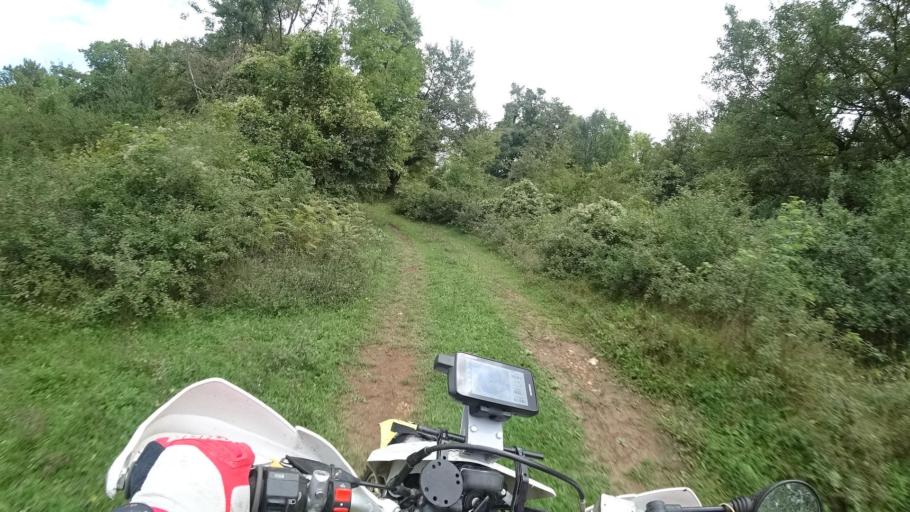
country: BA
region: Republika Srpska
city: Bronzani Majdan
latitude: 44.6468
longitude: 17.0215
